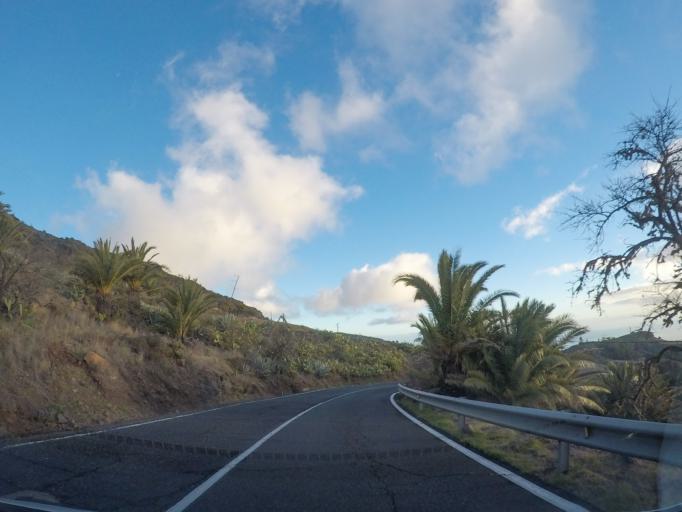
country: ES
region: Canary Islands
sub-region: Provincia de Santa Cruz de Tenerife
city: Alajero
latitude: 28.0748
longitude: -17.2390
